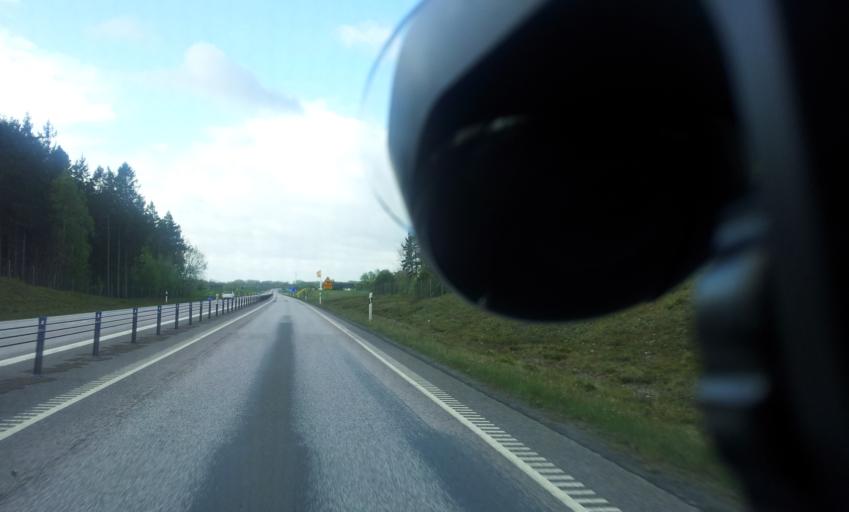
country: SE
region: Kalmar
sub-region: Torsas Kommun
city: Torsas
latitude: 56.4609
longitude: 16.0784
